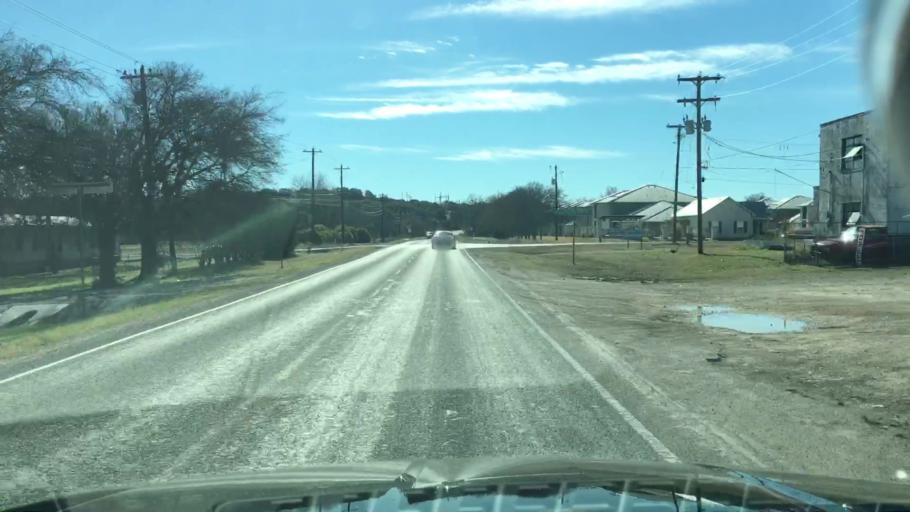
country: US
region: Texas
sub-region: Blanco County
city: Blanco
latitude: 30.0905
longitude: -98.4156
